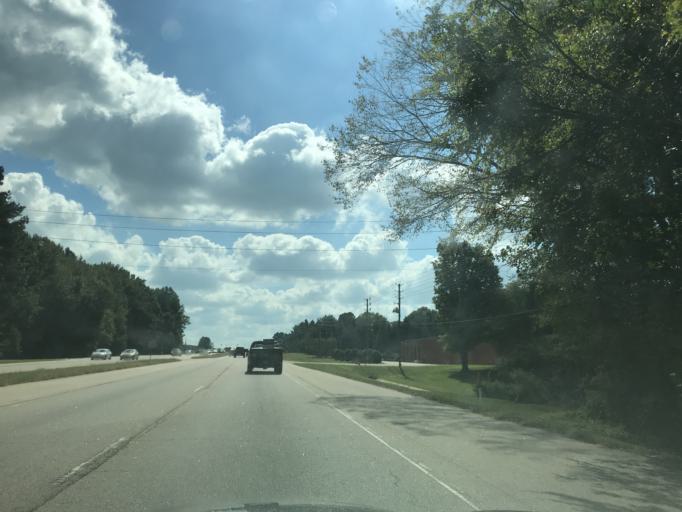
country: US
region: North Carolina
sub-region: Wake County
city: Wake Forest
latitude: 35.9032
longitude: -78.5580
